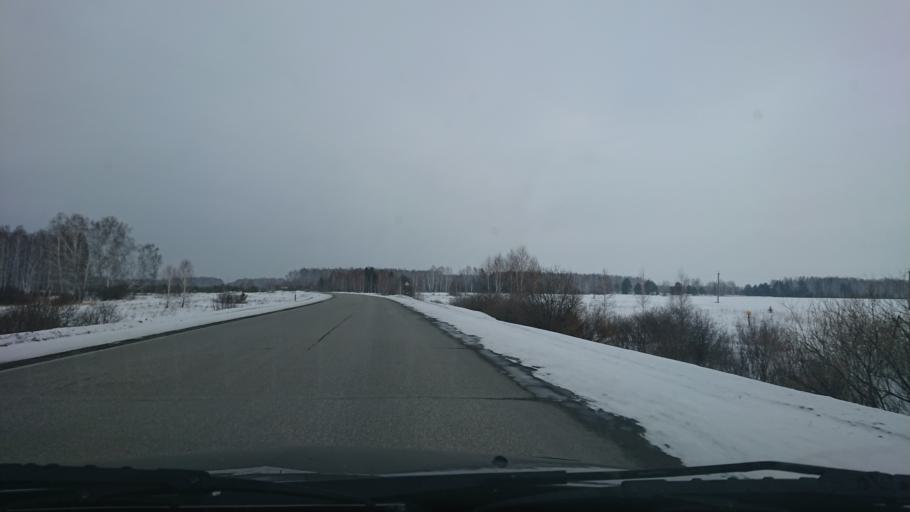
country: RU
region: Chelyabinsk
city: Tyubuk
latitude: 55.9746
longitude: 60.8536
